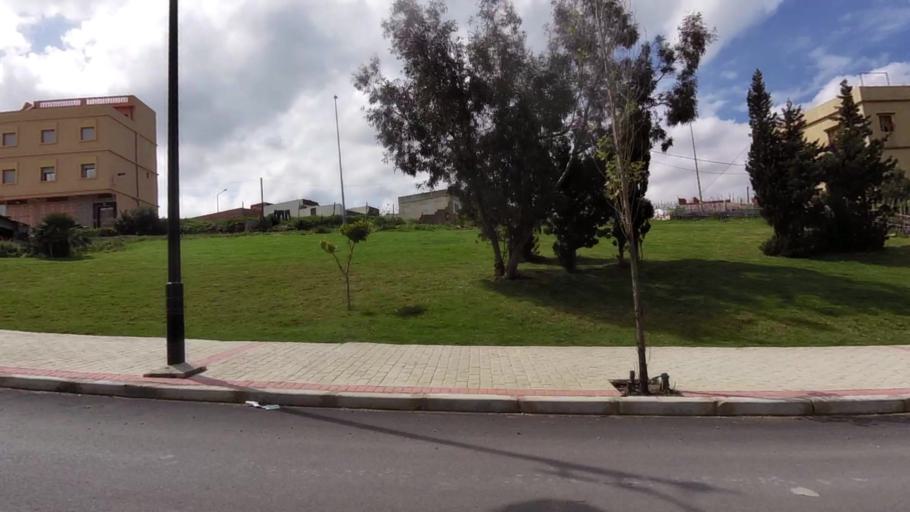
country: MA
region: Tanger-Tetouan
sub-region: Tanger-Assilah
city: Tangier
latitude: 35.7762
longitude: -5.7514
